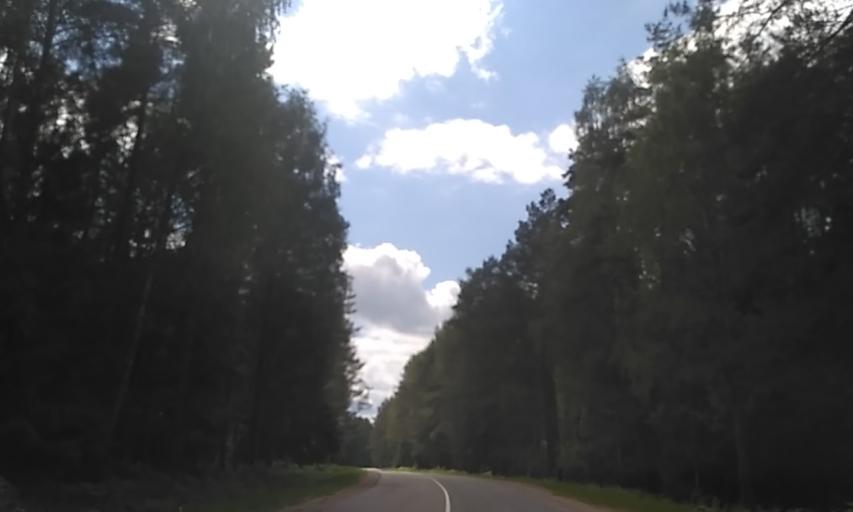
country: BY
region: Minsk
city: Khalopyenichy
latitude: 54.5163
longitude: 29.0687
